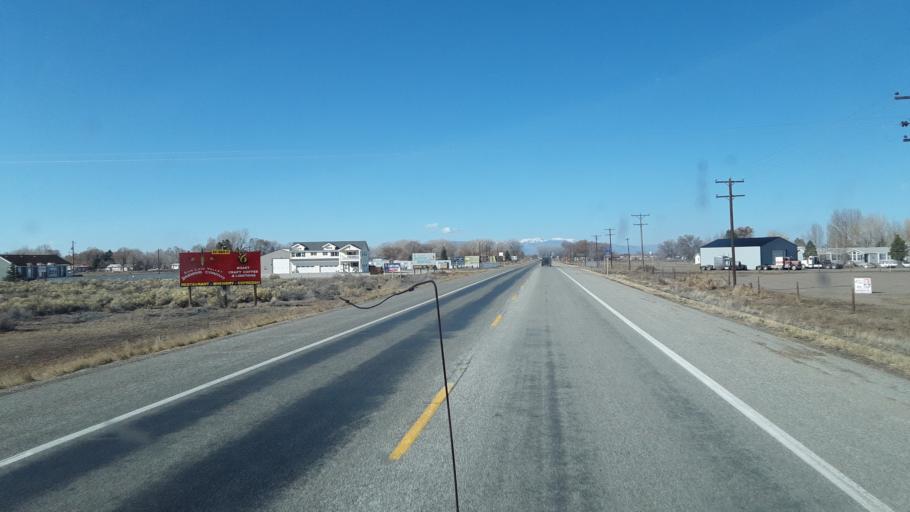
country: US
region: Colorado
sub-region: Alamosa County
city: Alamosa East
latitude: 37.4734
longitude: -105.8137
